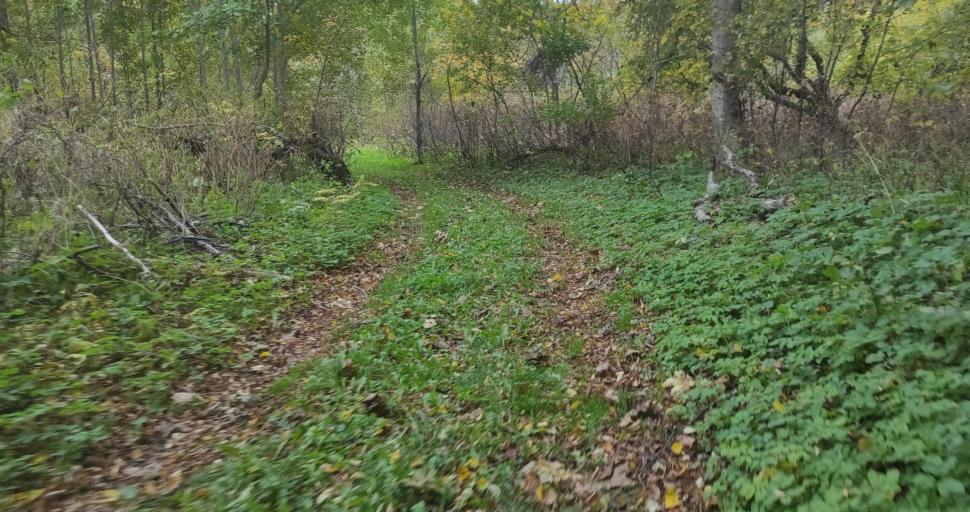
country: LV
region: Kandava
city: Kandava
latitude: 57.0165
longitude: 22.7574
